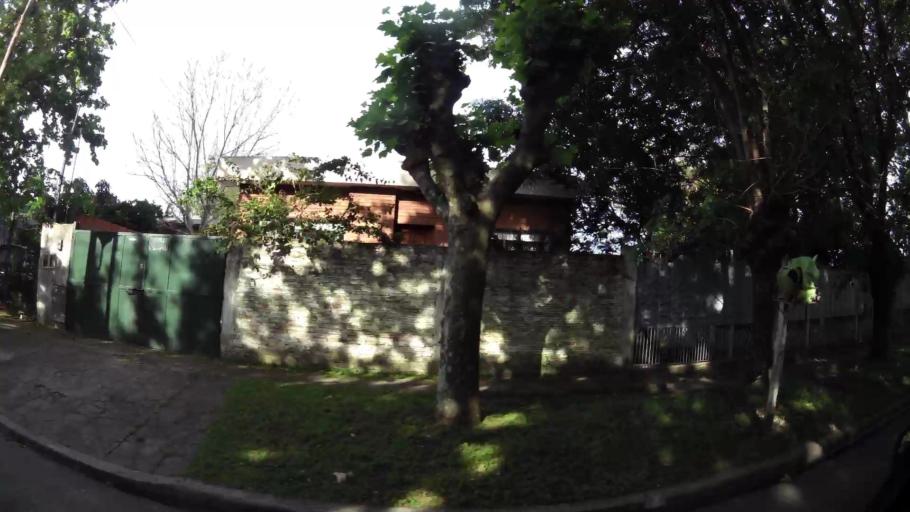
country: AR
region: Buenos Aires
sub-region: Partido de Quilmes
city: Quilmes
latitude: -34.7409
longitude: -58.2647
